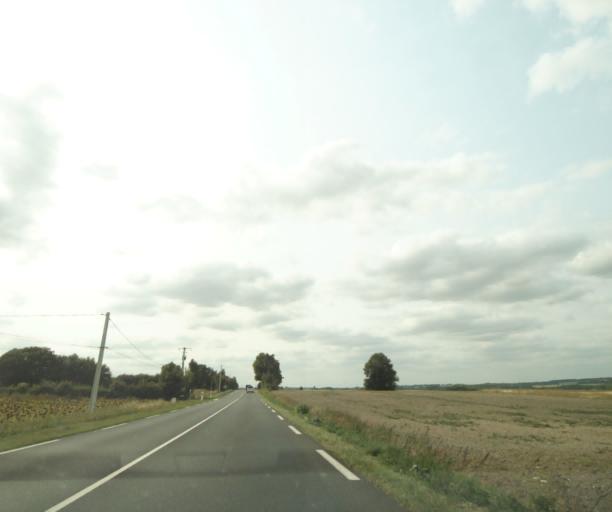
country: FR
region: Centre
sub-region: Departement de l'Indre
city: Clion
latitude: 46.9221
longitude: 1.2980
